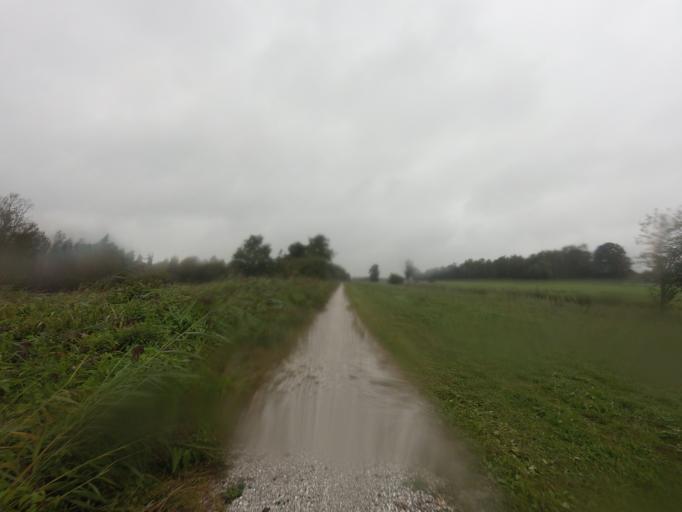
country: NL
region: Friesland
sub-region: Gemeente Smallingerland
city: Oudega
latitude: 53.0985
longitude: 5.9819
